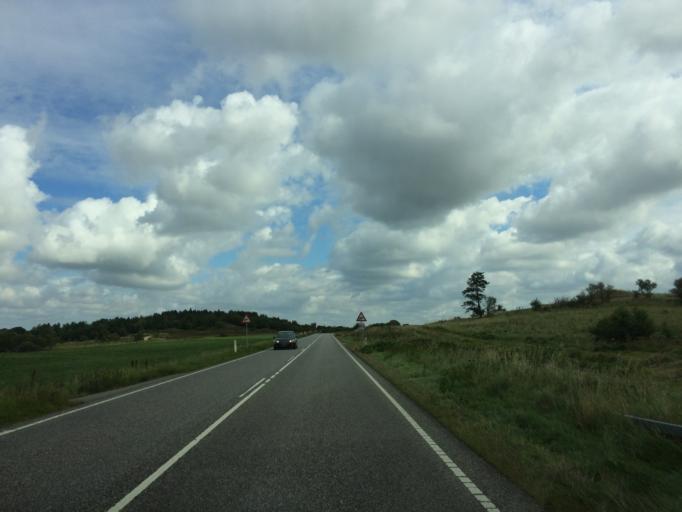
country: DK
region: Central Jutland
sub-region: Holstebro Kommune
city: Holstebro
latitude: 56.3284
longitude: 8.4763
